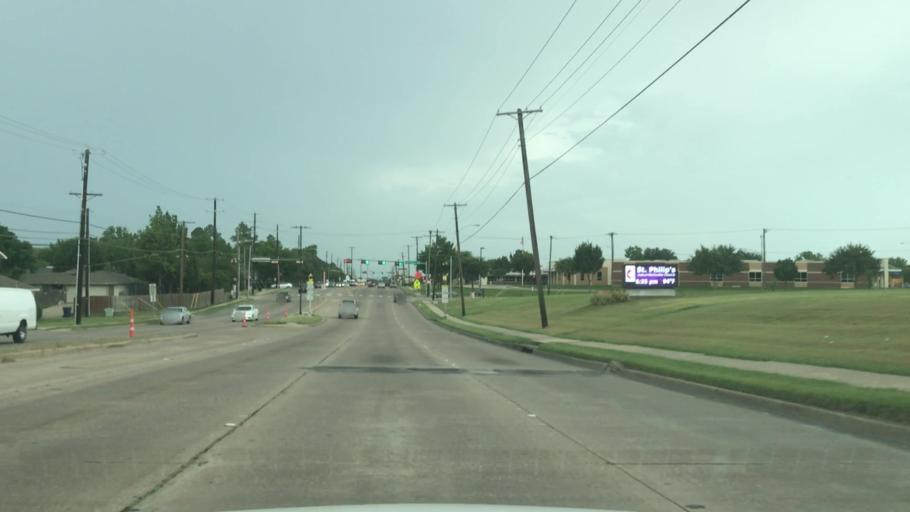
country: US
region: Texas
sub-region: Dallas County
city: Garland
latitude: 32.8698
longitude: -96.6112
